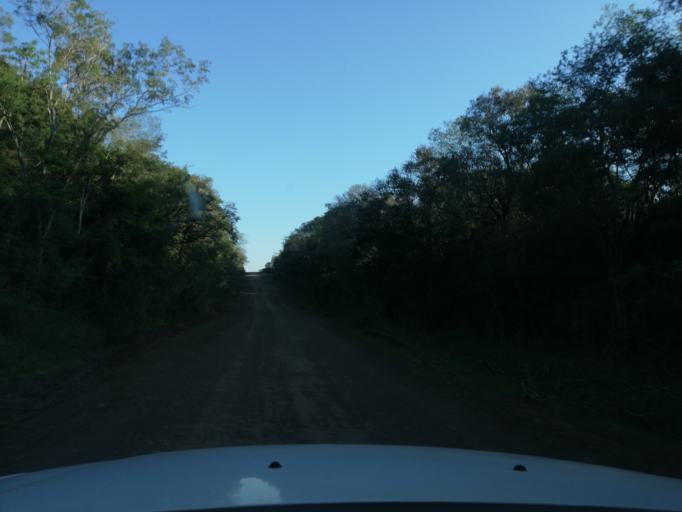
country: AR
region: Misiones
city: Cerro Cora
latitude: -27.5805
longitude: -55.6863
